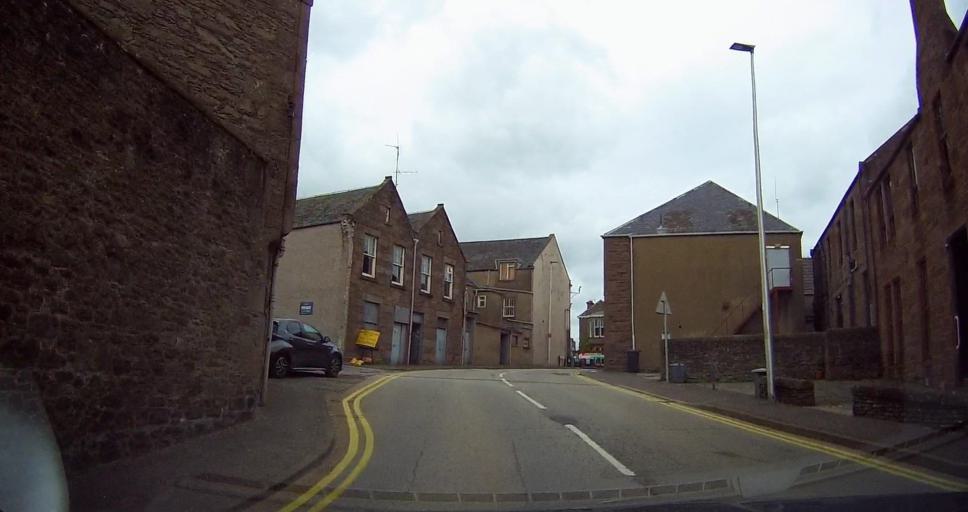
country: GB
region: Scotland
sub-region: Angus
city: Forfar
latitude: 56.6441
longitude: -2.8848
